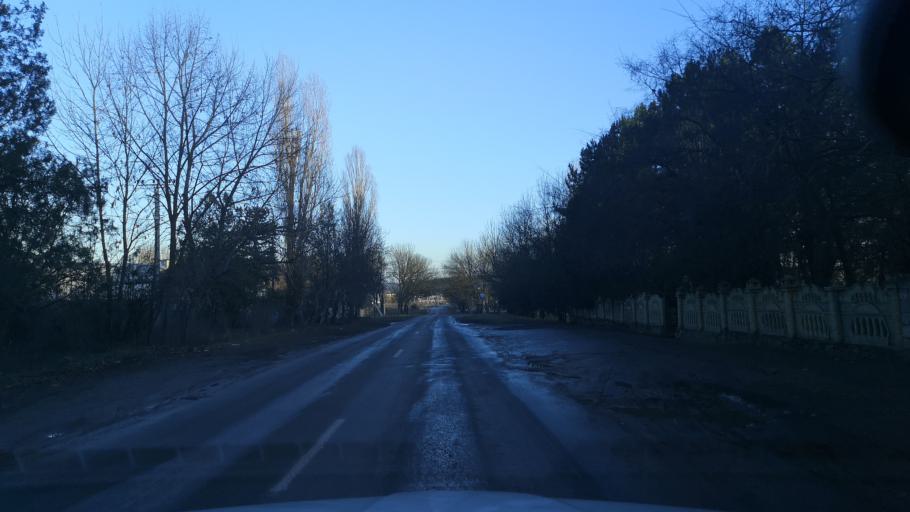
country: MD
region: Orhei
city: Orhei
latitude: 47.2878
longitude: 28.8594
